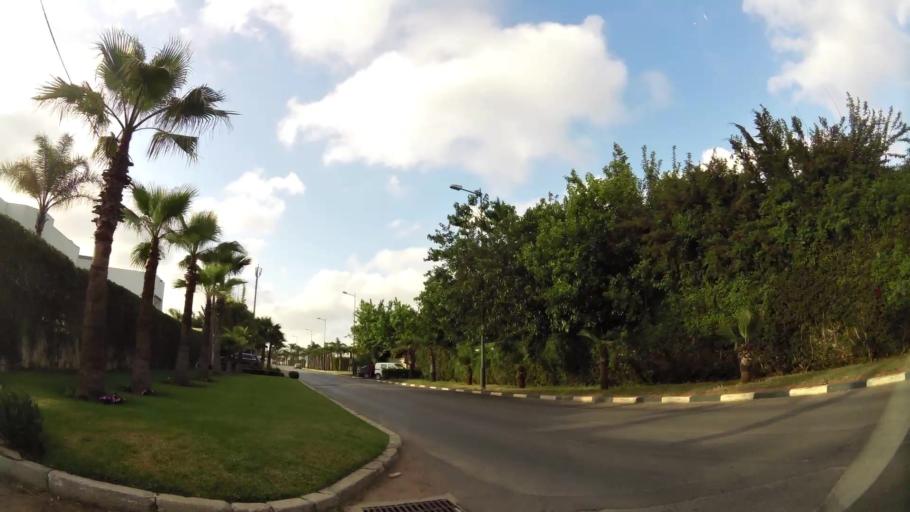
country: MA
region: Rabat-Sale-Zemmour-Zaer
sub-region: Rabat
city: Rabat
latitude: 33.9570
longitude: -6.8418
